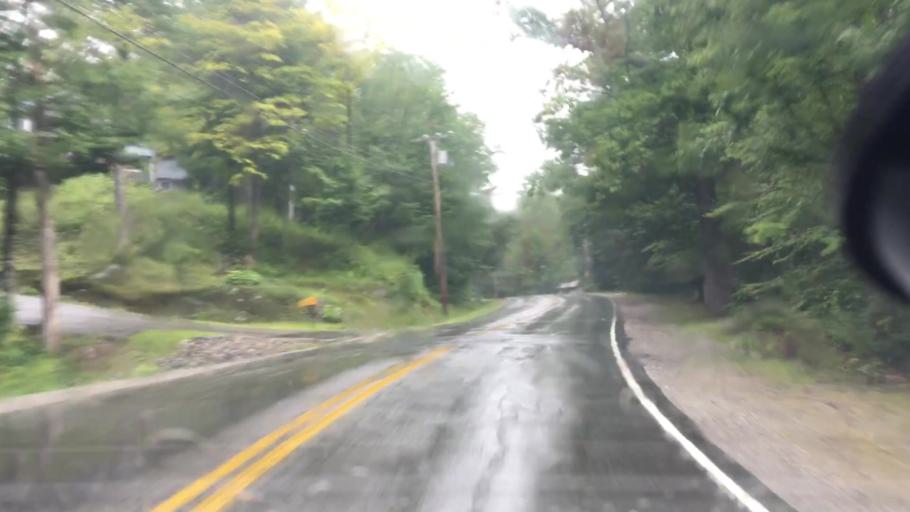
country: US
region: Maine
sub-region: Oxford County
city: Lovell
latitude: 44.2583
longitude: -70.8419
